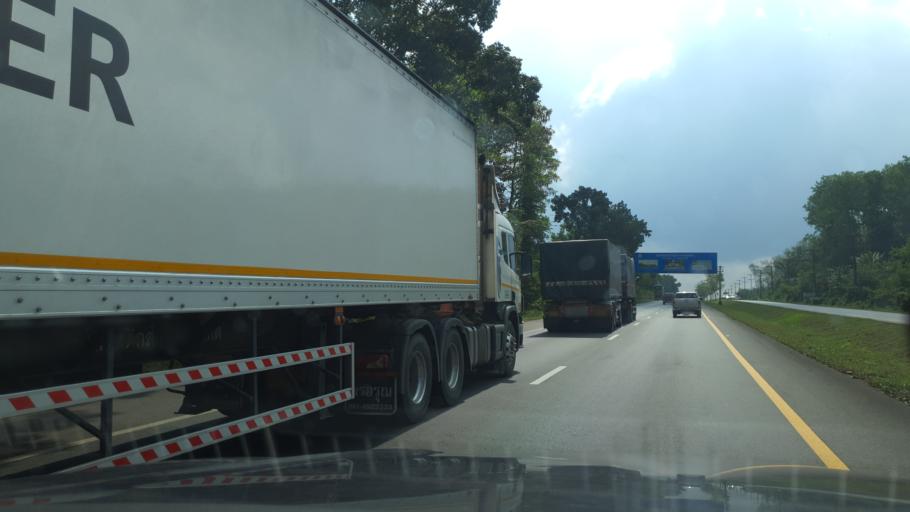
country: TH
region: Chumphon
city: Tha Sae
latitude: 10.7722
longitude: 99.1941
